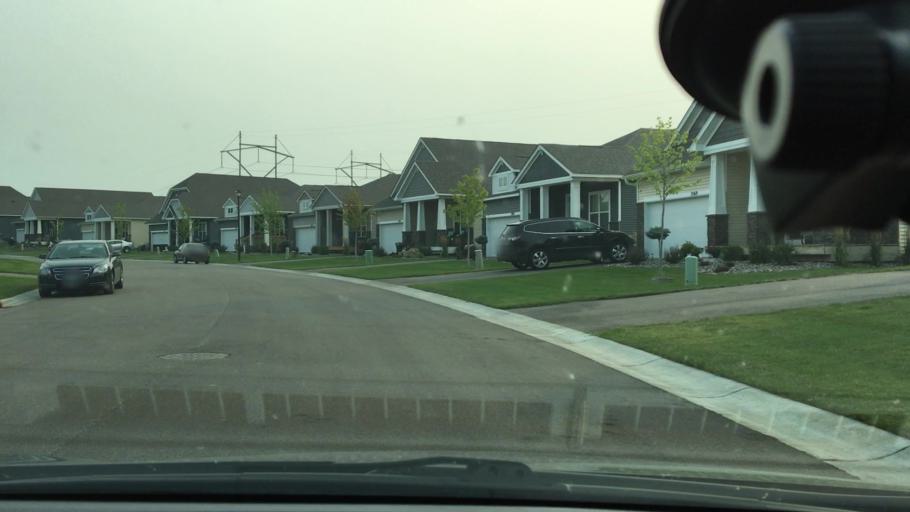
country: US
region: Minnesota
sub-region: Wright County
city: Saint Michael
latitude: 45.2046
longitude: -93.6836
